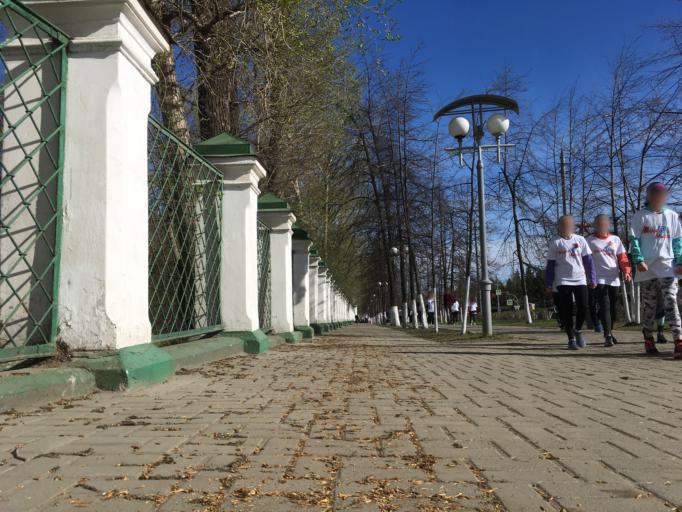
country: RU
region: Tomsk
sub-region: Tomskiy Rayon
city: Tomsk
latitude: 56.4682
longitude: 84.9509
